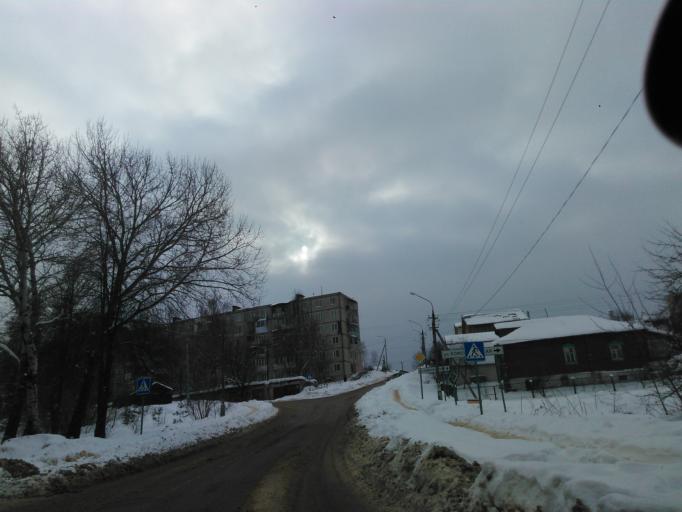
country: RU
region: Moskovskaya
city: Yakhroma
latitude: 56.2846
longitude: 37.4821
